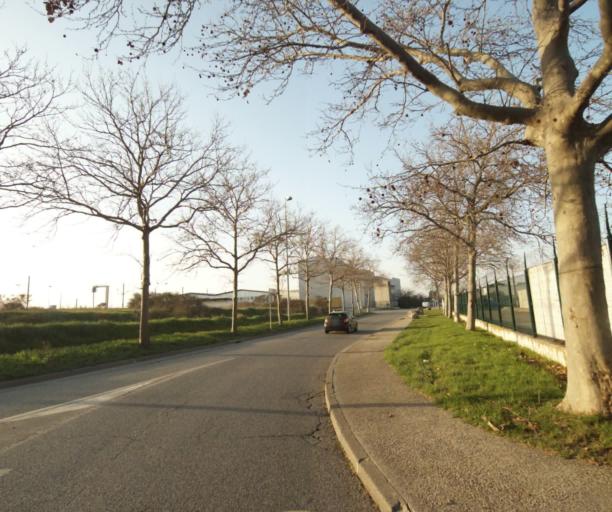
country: FR
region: Provence-Alpes-Cote d'Azur
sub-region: Departement des Bouches-du-Rhone
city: Saint-Victoret
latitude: 43.4226
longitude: 5.2514
